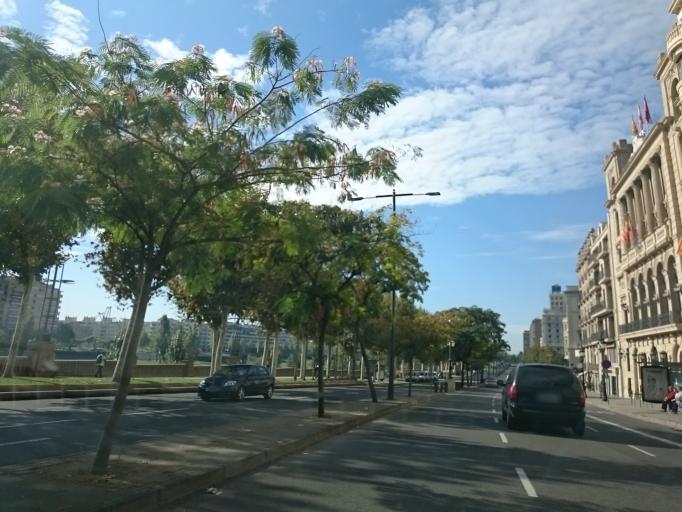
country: ES
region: Catalonia
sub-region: Provincia de Lleida
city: Lleida
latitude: 41.6149
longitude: 0.6274
